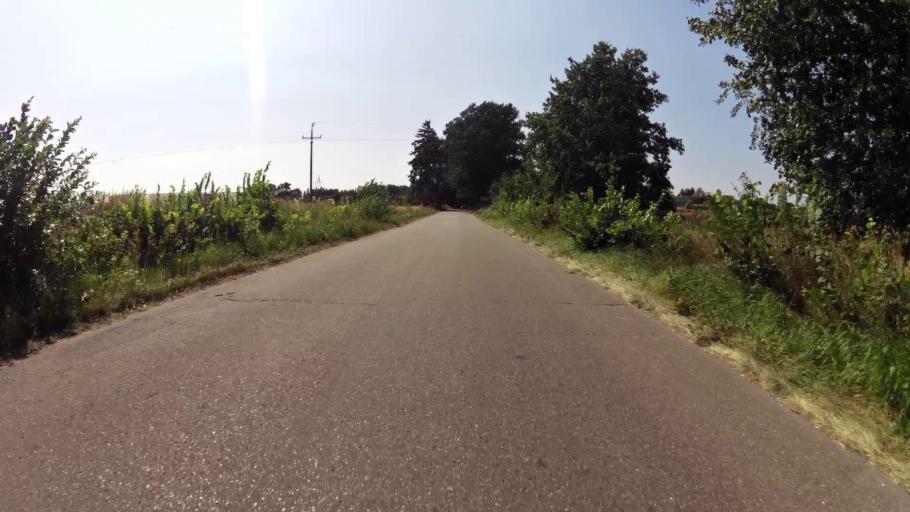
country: PL
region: West Pomeranian Voivodeship
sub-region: Powiat walecki
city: Walcz
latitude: 53.2052
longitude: 16.4966
